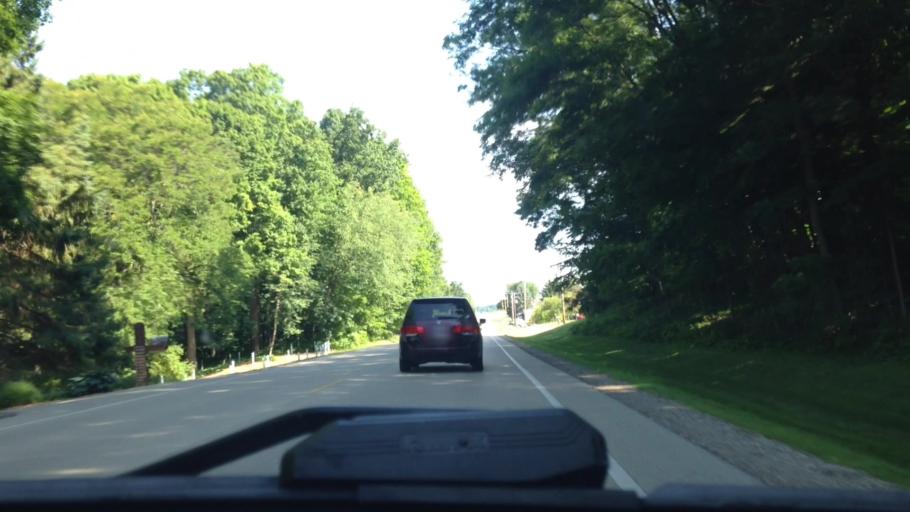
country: US
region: Wisconsin
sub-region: Washington County
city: West Bend
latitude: 43.4001
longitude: -88.2410
